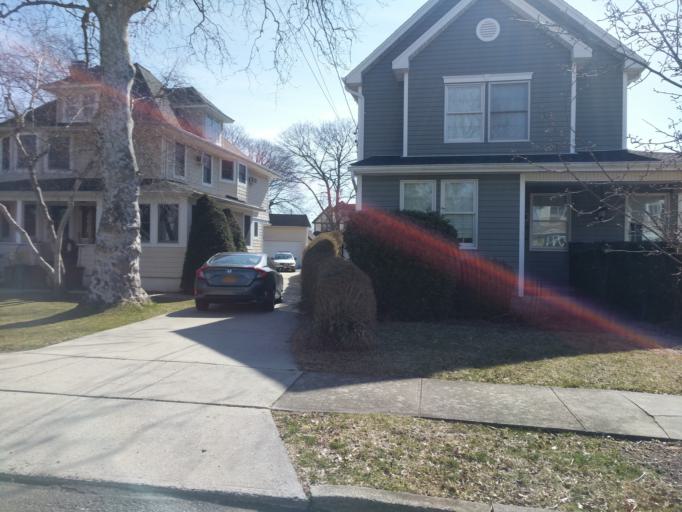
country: US
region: New York
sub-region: Nassau County
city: Lynbrook
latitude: 40.6501
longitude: -73.6738
